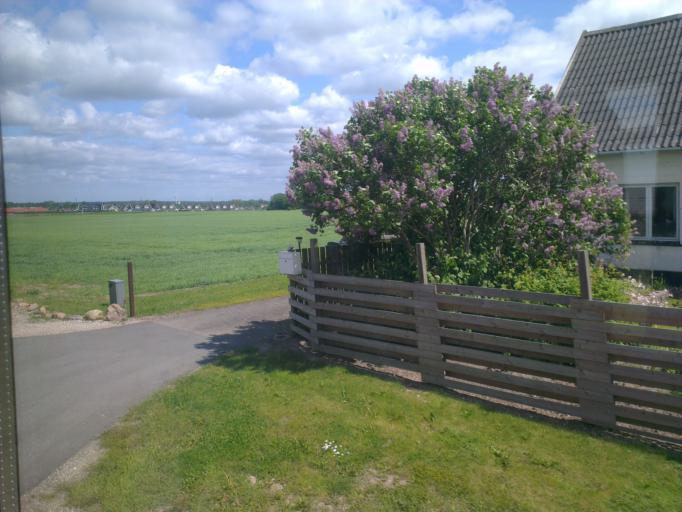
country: DK
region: Capital Region
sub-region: Frederikssund Kommune
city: Slangerup
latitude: 55.8772
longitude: 12.1930
